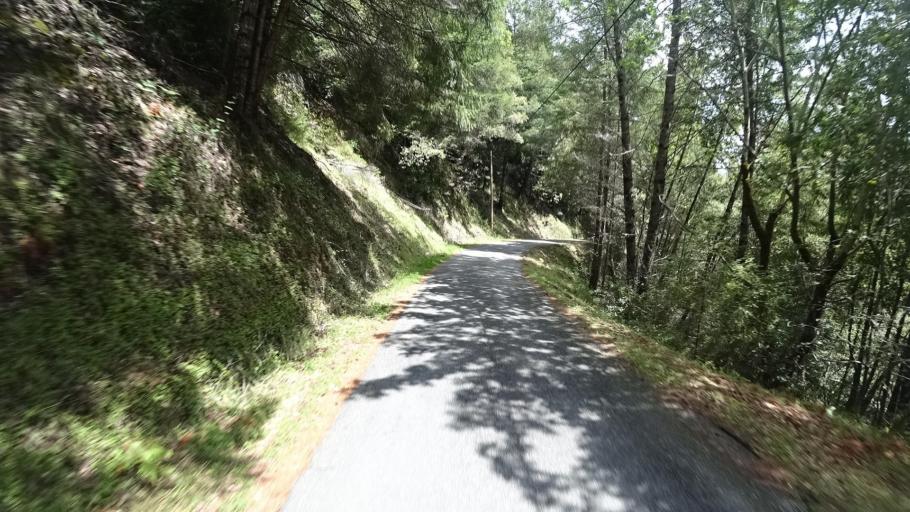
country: US
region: California
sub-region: Humboldt County
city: Blue Lake
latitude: 40.7583
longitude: -123.9154
